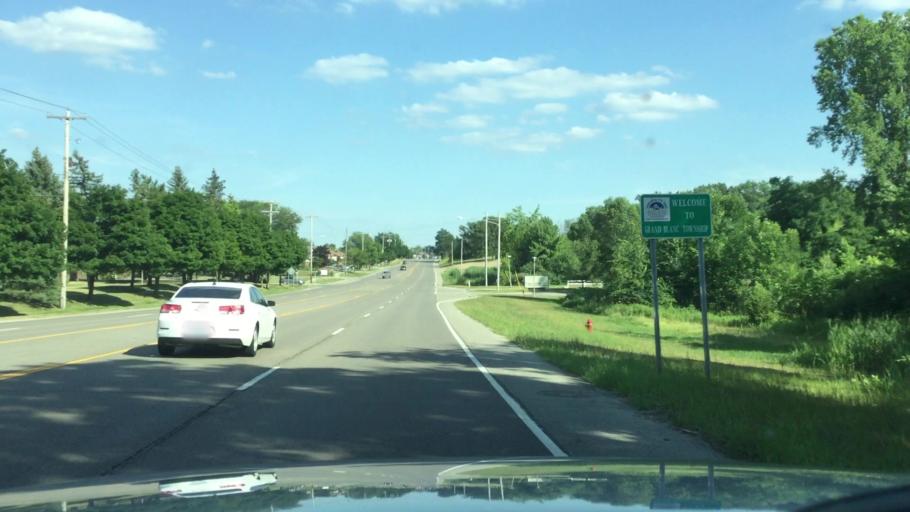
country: US
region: Michigan
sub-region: Genesee County
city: Grand Blanc
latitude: 42.9154
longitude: -83.6136
